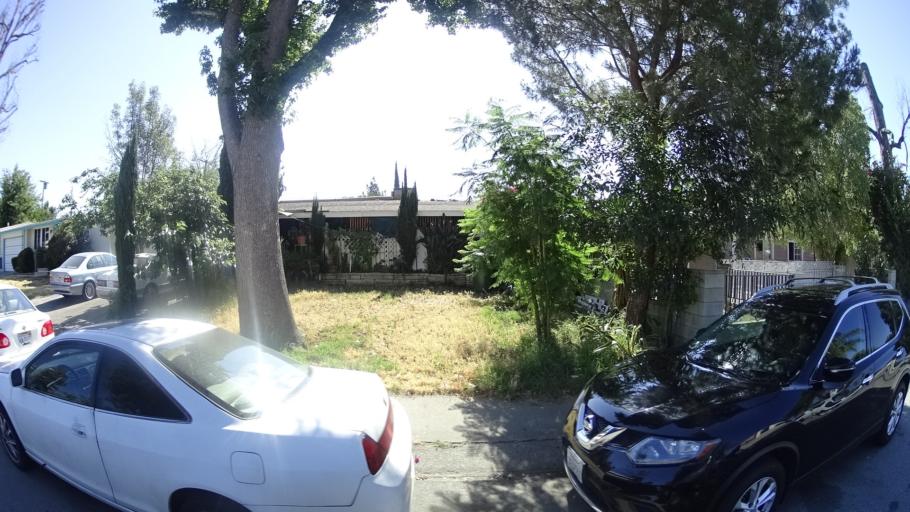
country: US
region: California
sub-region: Los Angeles County
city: Van Nuys
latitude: 34.2245
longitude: -118.4350
